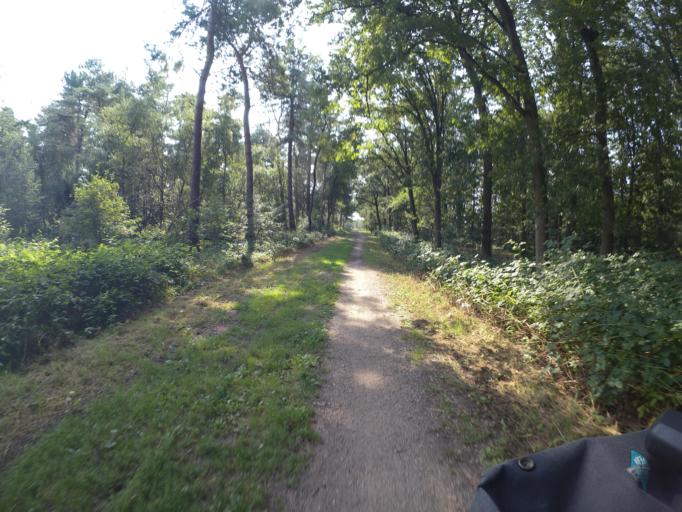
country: NL
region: Limburg
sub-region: Gemeente Venray
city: Venray
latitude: 51.4702
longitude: 5.9018
